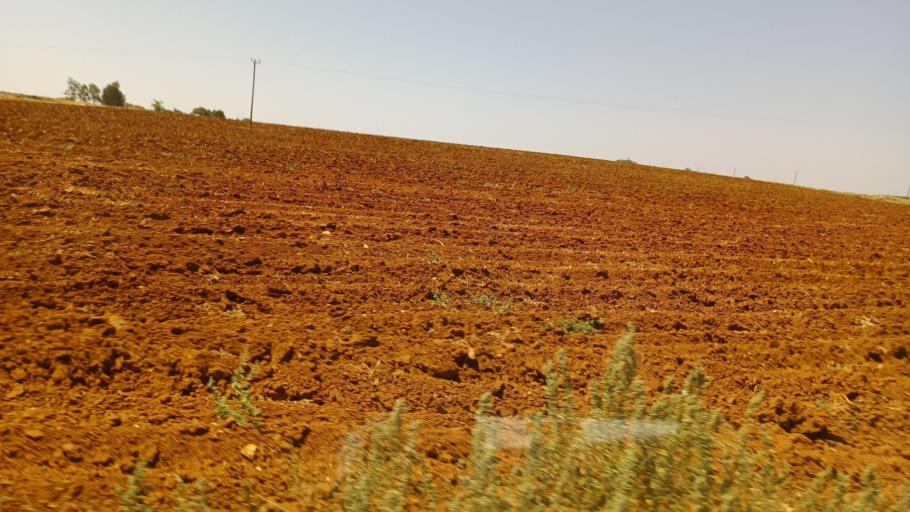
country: CY
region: Ammochostos
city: Liopetri
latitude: 35.0319
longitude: 33.8990
